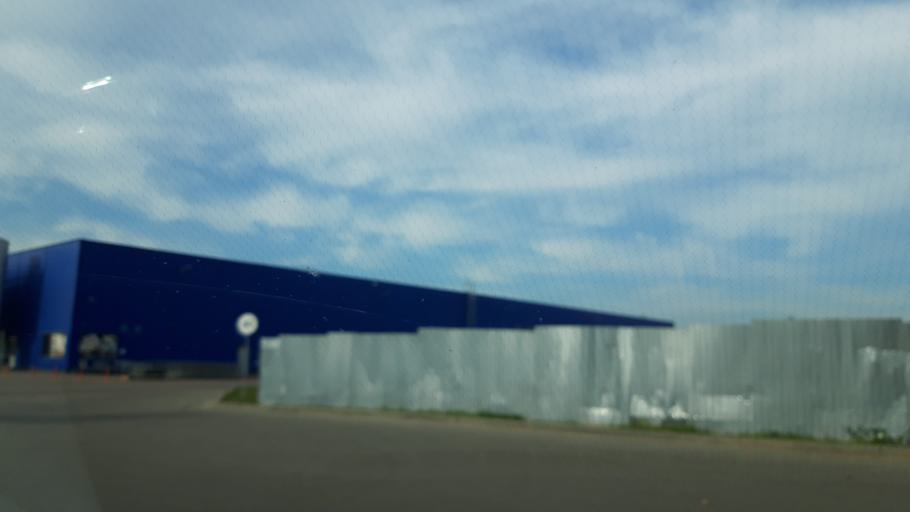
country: RU
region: Moskovskaya
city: Skhodnya
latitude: 55.9813
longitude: 37.3004
